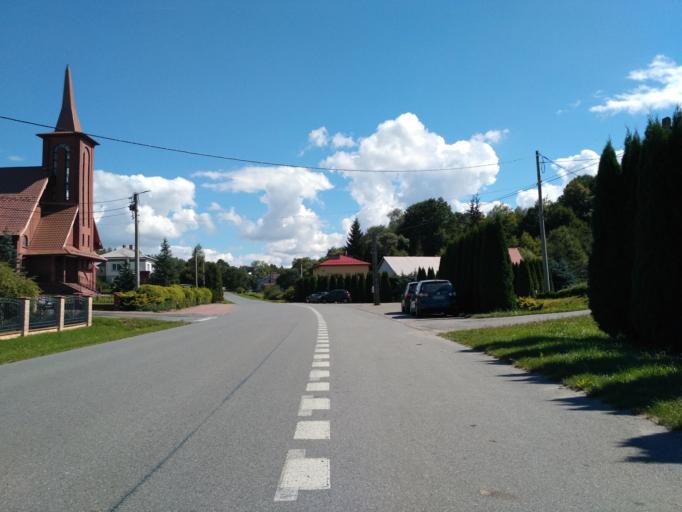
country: PL
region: Subcarpathian Voivodeship
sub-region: Powiat jasielski
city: Skolyszyn
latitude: 49.7914
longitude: 21.3337
